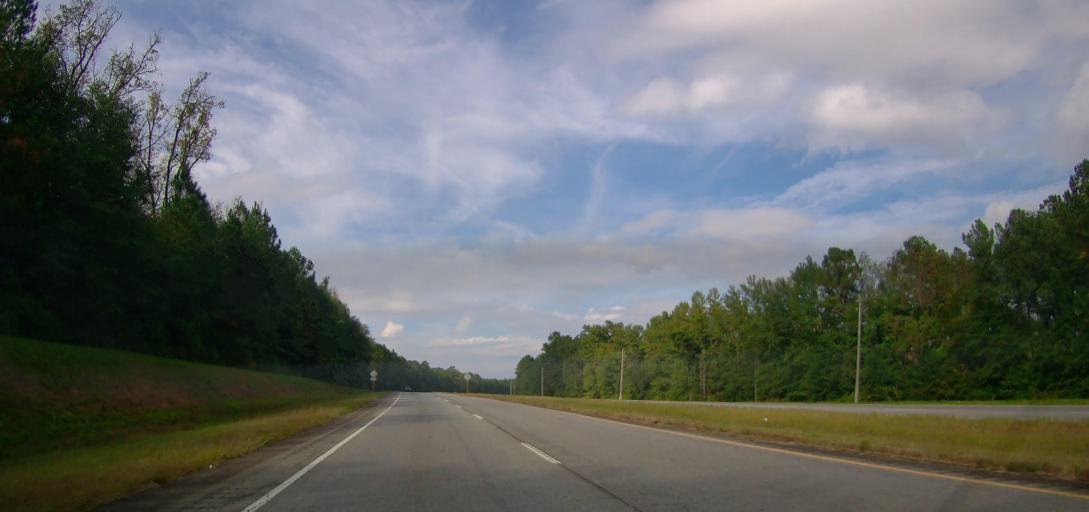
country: US
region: Georgia
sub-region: Thomas County
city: Thomasville
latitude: 30.8537
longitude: -84.0070
